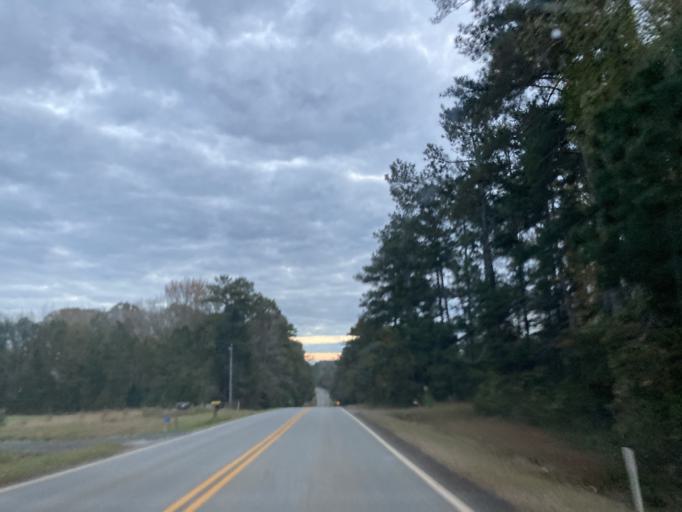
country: US
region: Georgia
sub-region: Jones County
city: Gray
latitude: 32.9782
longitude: -83.5057
